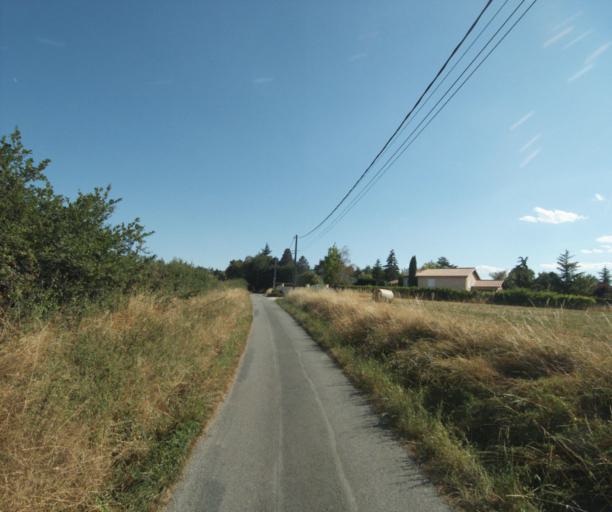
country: FR
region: Rhone-Alpes
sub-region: Departement du Rhone
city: La Tour-de-Salvagny
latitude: 45.8314
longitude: 4.7229
